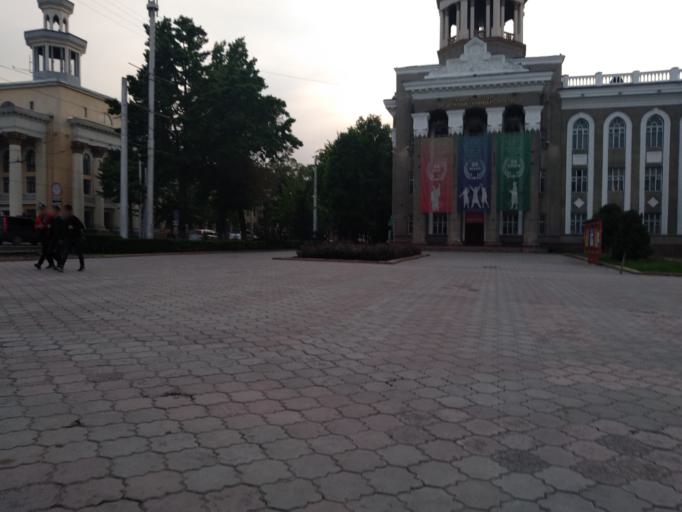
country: KG
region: Chuy
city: Bishkek
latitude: 42.8769
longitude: 74.5867
